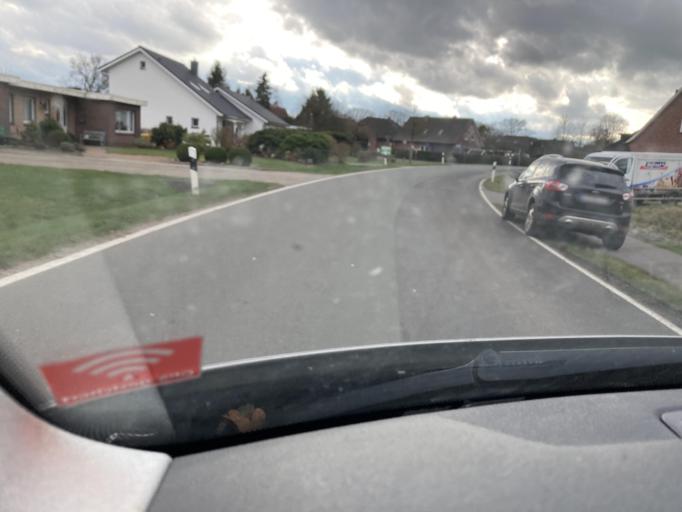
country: DE
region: Lower Saxony
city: Zetel
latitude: 53.4350
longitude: 7.9272
